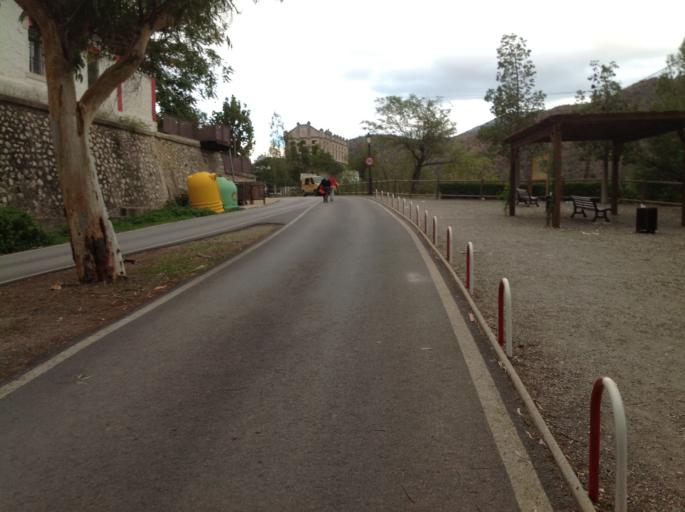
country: ES
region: Andalusia
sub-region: Provincia de Malaga
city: Carratraca
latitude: 36.9076
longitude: -4.7596
